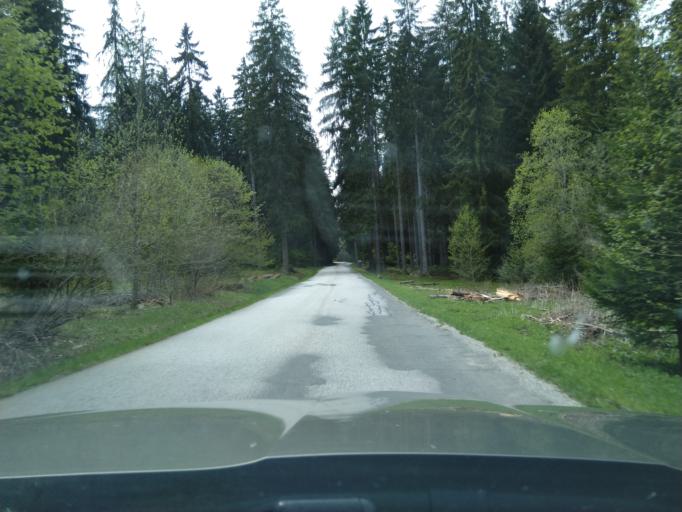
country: CZ
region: Jihocesky
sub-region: Okres Prachatice
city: Vimperk
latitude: 49.0235
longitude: 13.7473
